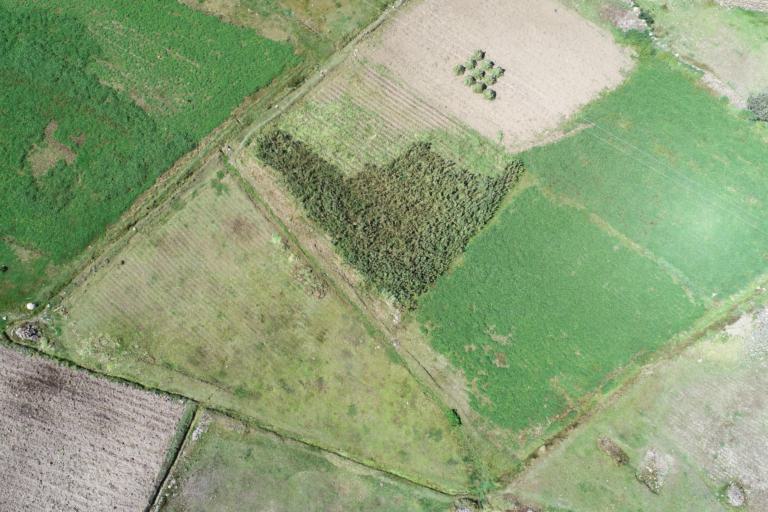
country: BO
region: La Paz
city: Achacachi
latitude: -16.0204
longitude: -68.6155
